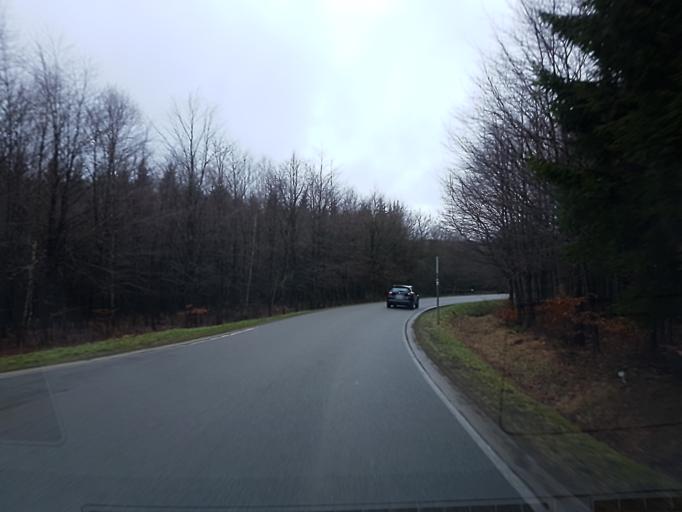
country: BE
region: Wallonia
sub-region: Province de Liege
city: Malmedy
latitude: 50.4652
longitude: 6.0470
